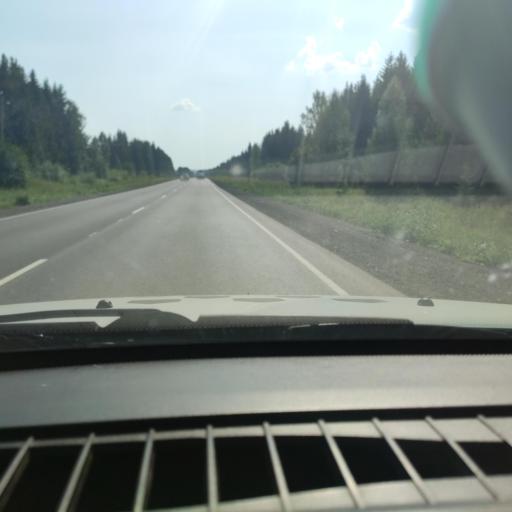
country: RU
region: Perm
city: Orda
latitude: 57.2202
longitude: 56.9497
